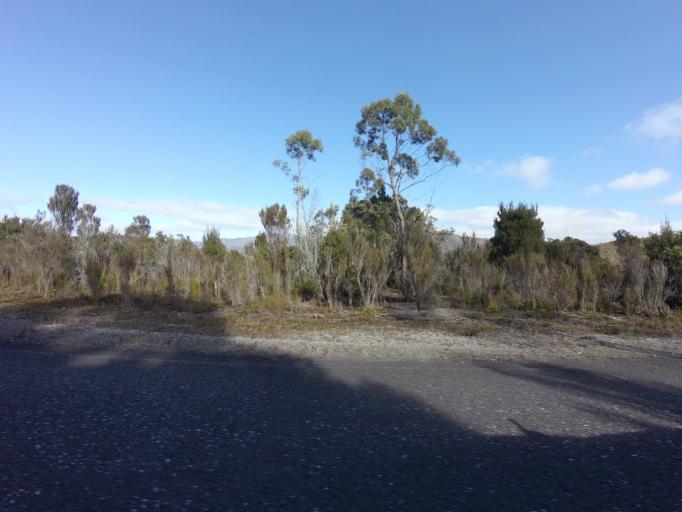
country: AU
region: Tasmania
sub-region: West Coast
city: Queenstown
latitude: -42.7761
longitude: 146.0573
